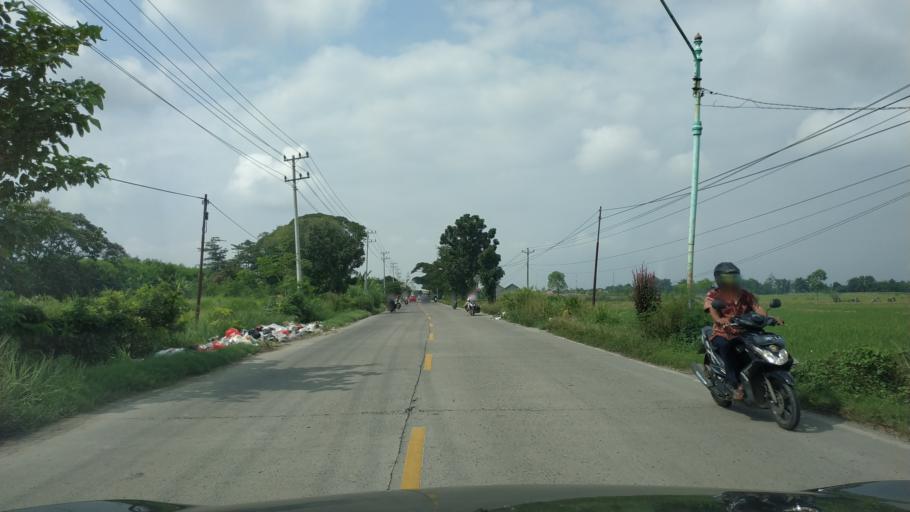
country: ID
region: Central Java
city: Ketanggungan
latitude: -6.9115
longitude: 108.8897
